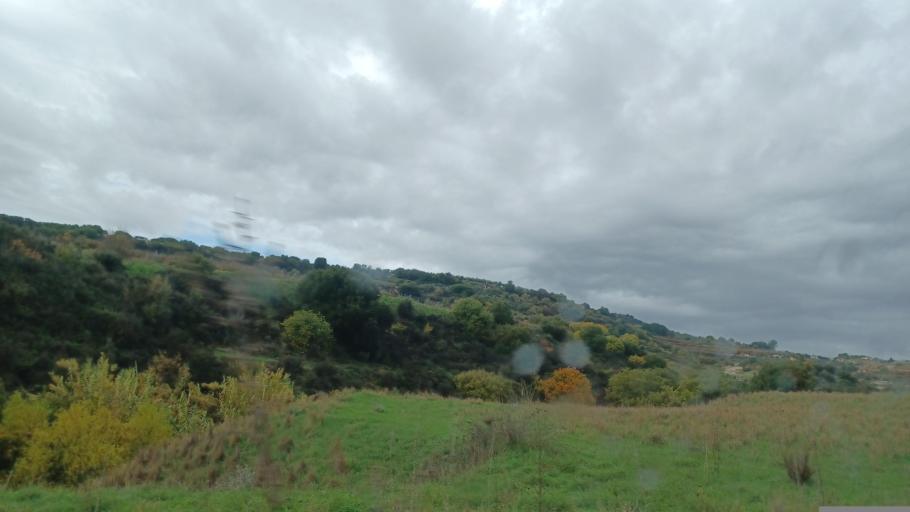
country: CY
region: Pafos
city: Mesogi
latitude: 34.8664
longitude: 32.5352
